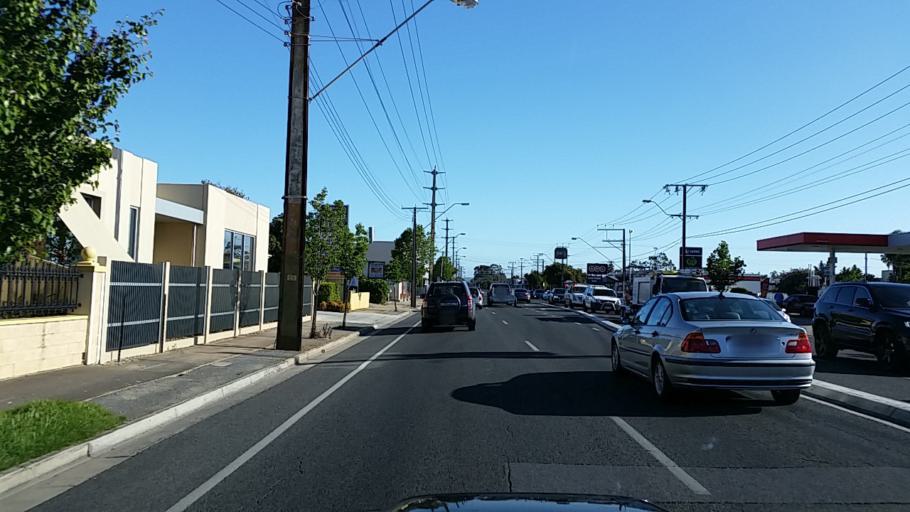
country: AU
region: South Australia
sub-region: City of West Torrens
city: Plympton
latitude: -34.9362
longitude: 138.5528
